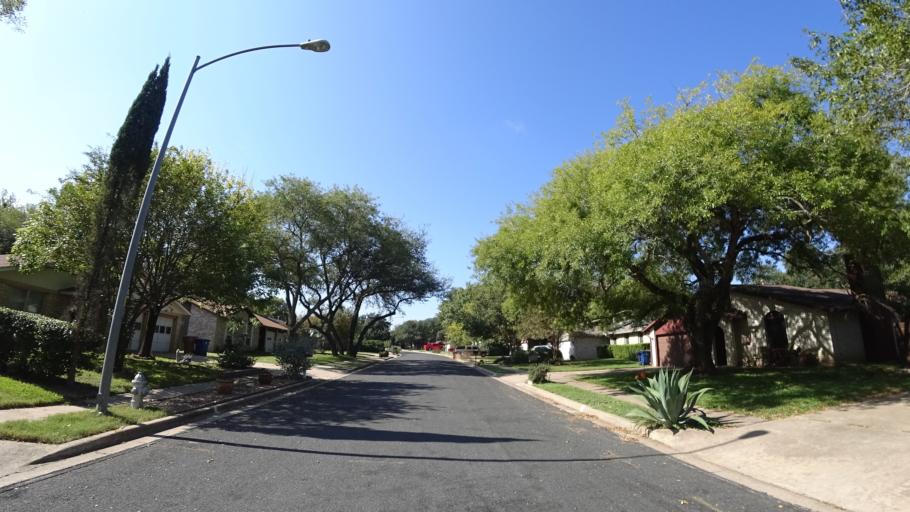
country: US
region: Texas
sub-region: Travis County
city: Shady Hollow
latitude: 30.2135
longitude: -97.8163
